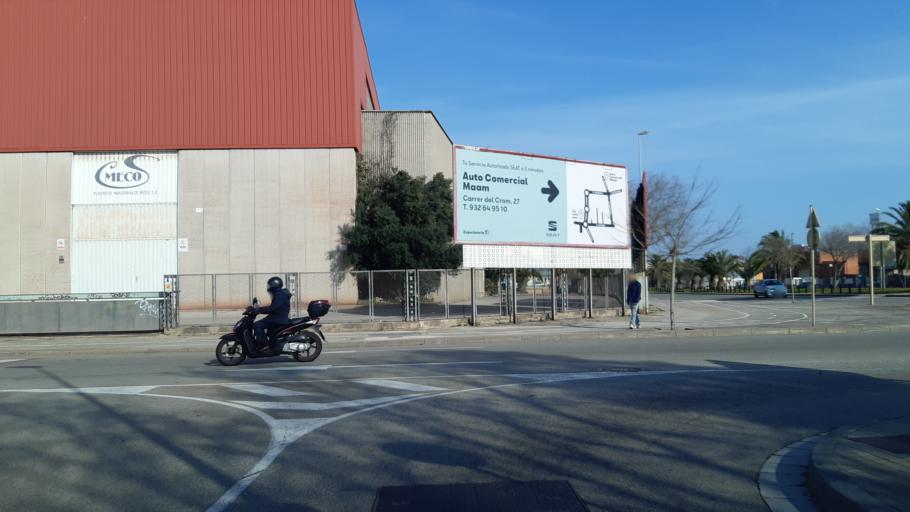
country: ES
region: Catalonia
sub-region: Provincia de Barcelona
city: Cornella de Llobregat
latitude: 41.3543
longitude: 2.0919
